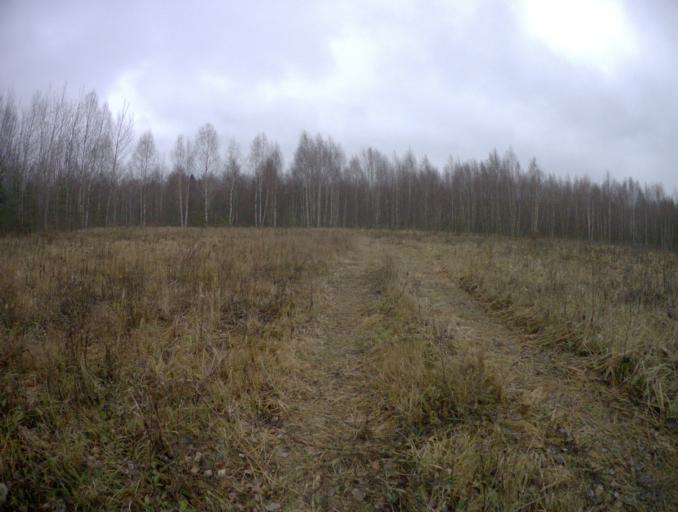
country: RU
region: Vladimir
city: Golovino
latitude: 56.0015
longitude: 40.5440
